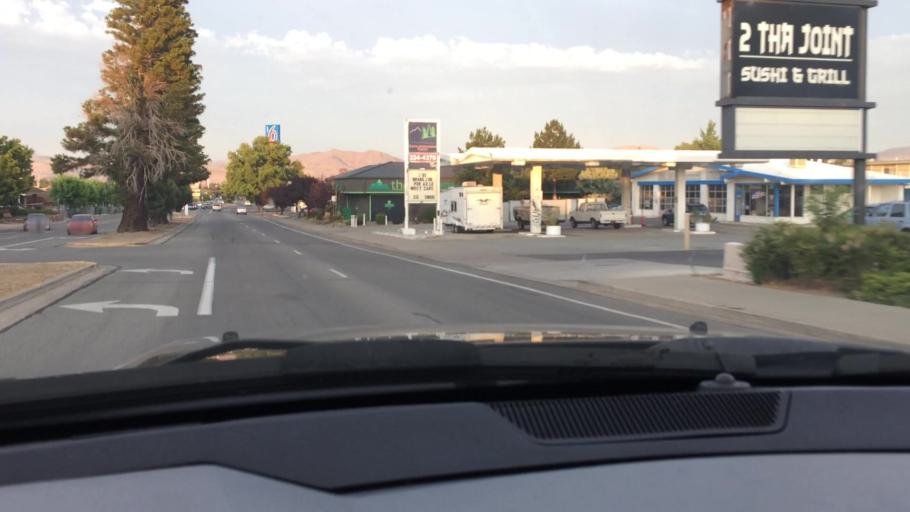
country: US
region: Nevada
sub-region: Washoe County
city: Reno
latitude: 39.5056
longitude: -119.8063
